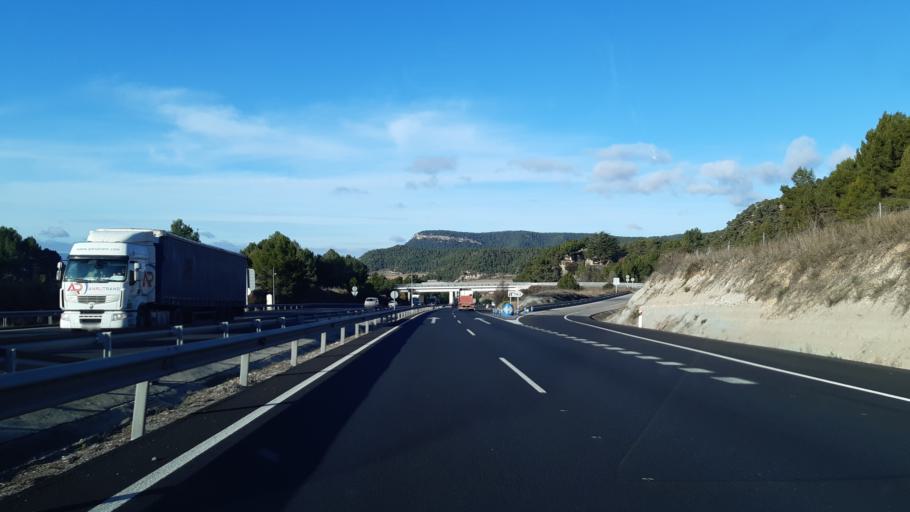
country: ES
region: Catalonia
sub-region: Provincia de Barcelona
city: Castelloli
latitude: 41.5973
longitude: 1.7141
